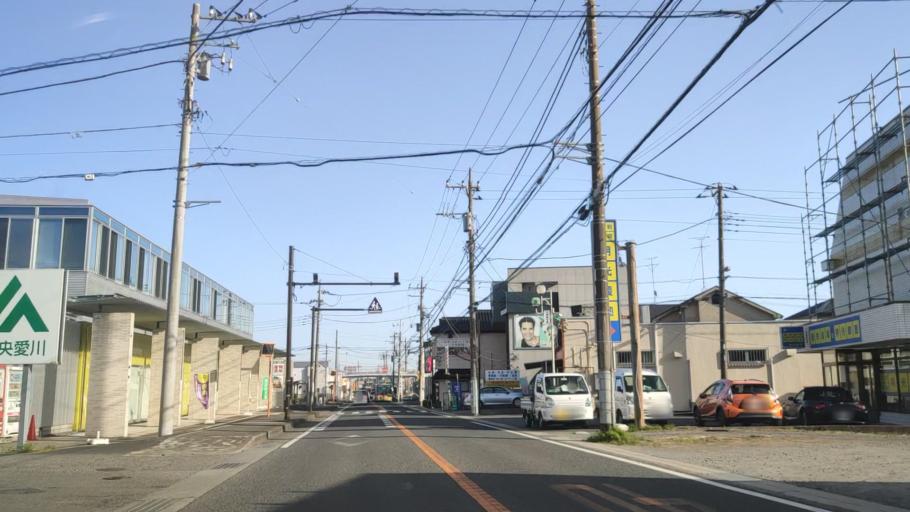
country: JP
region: Kanagawa
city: Zama
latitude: 35.5147
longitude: 139.3359
